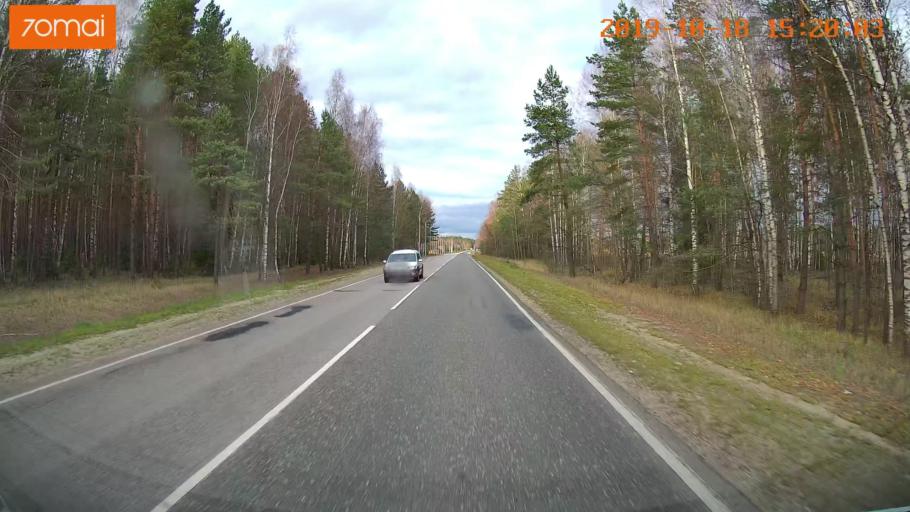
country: RU
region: Vladimir
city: Anopino
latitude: 55.6821
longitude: 40.7422
